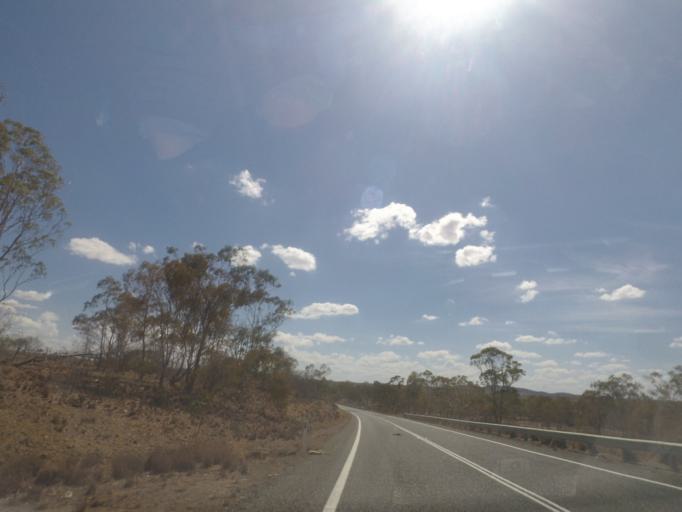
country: AU
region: Queensland
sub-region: Southern Downs
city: Warwick
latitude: -28.2054
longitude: 151.5721
